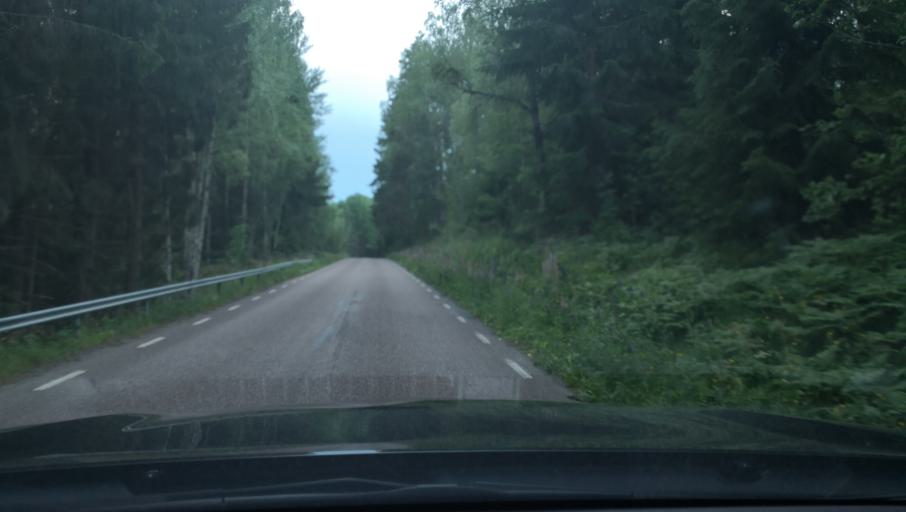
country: SE
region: Dalarna
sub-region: Smedjebackens Kommun
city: Smedjebacken
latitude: 60.0456
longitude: 15.5108
